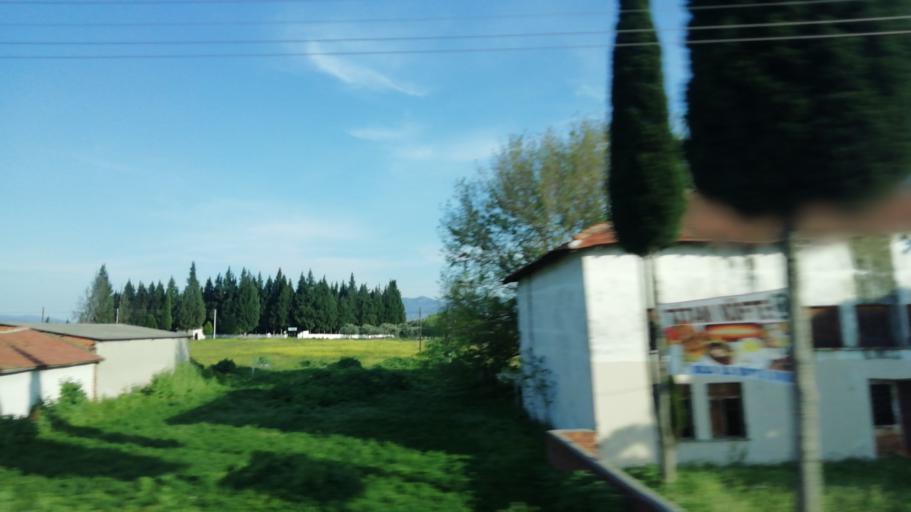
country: TR
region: Manisa
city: Saruhanli
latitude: 38.7530
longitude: 27.6275
